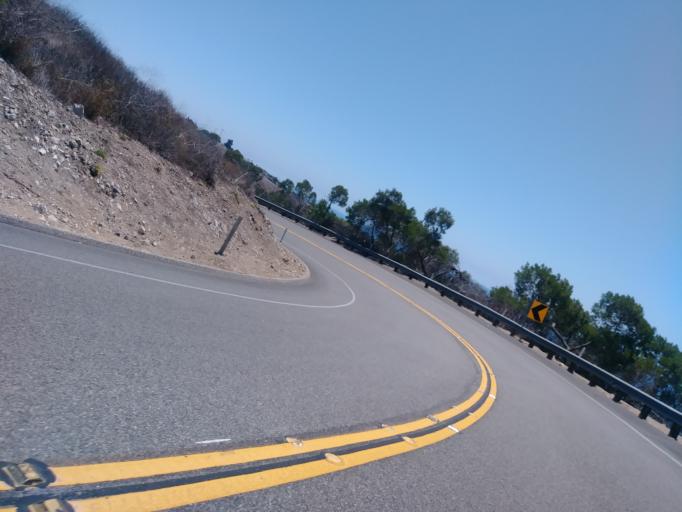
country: US
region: California
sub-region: Los Angeles County
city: Rolling Hills
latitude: 33.7297
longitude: -118.3315
